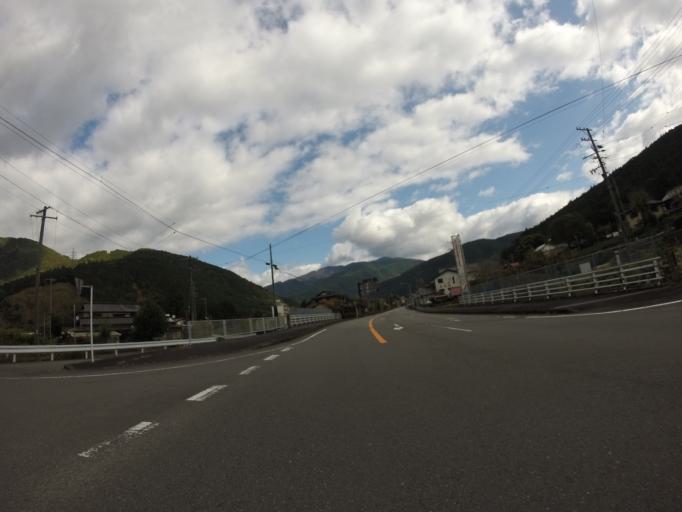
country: JP
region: Shizuoka
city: Fujieda
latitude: 35.1002
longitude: 138.1282
